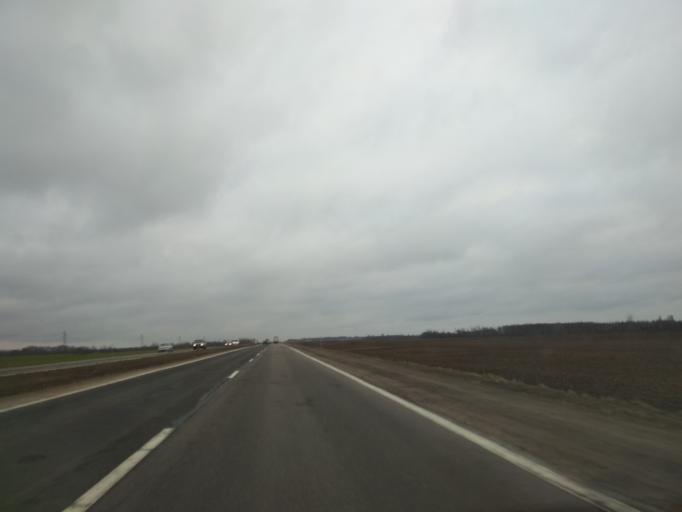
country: BY
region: Minsk
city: Dukora
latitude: 53.6509
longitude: 27.9713
